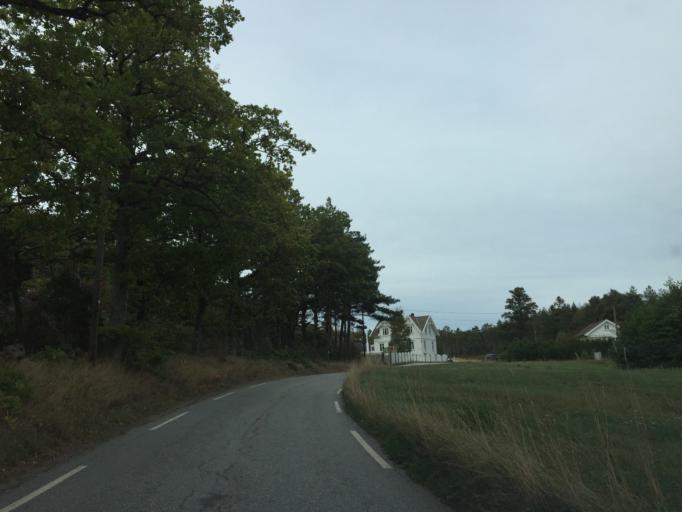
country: NO
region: Ostfold
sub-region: Hvaler
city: Skjaerhalden
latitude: 59.0492
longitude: 11.0445
